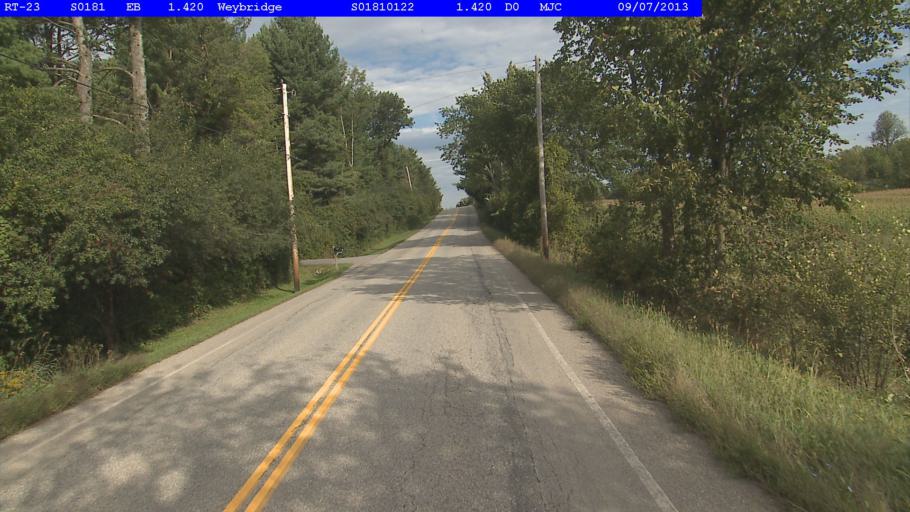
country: US
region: Vermont
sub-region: Addison County
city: Middlebury (village)
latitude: 44.0325
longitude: -73.2035
